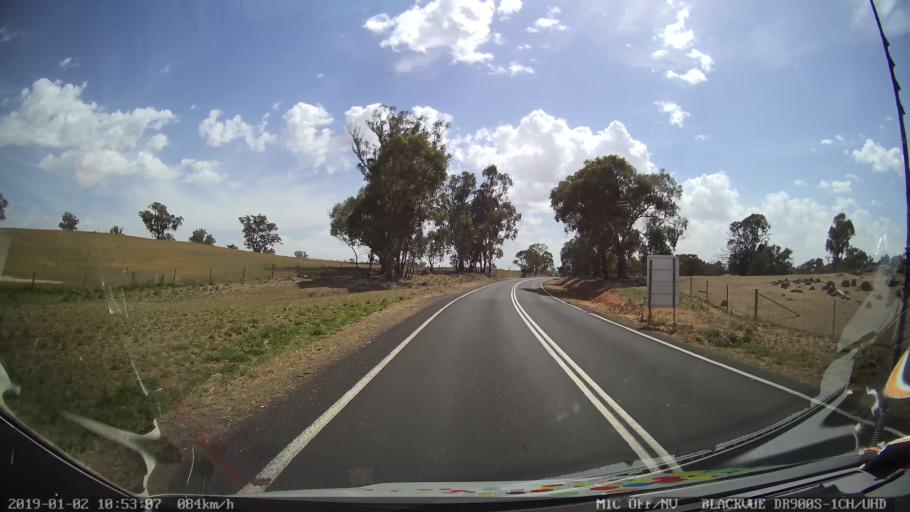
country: AU
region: New South Wales
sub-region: Cootamundra
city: Cootamundra
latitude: -34.6808
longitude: 148.2724
